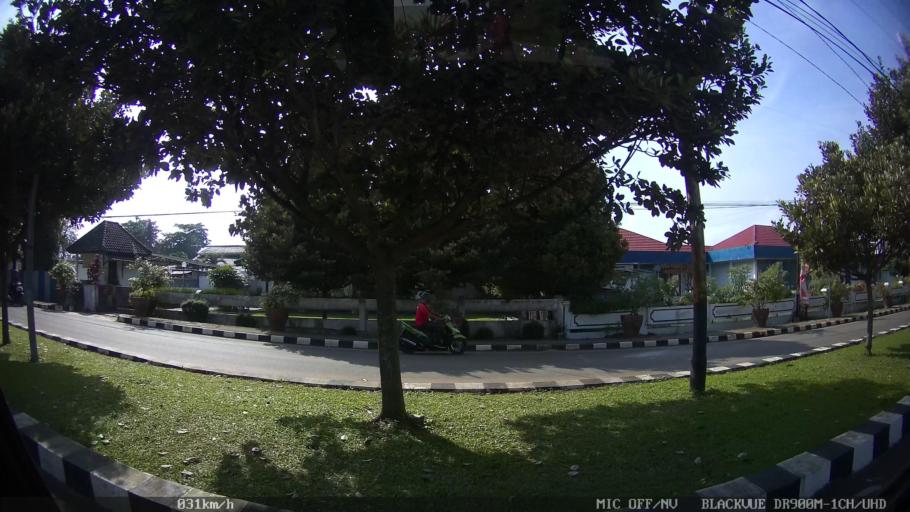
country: ID
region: Lampung
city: Kedaton
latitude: -5.3688
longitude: 105.2417
